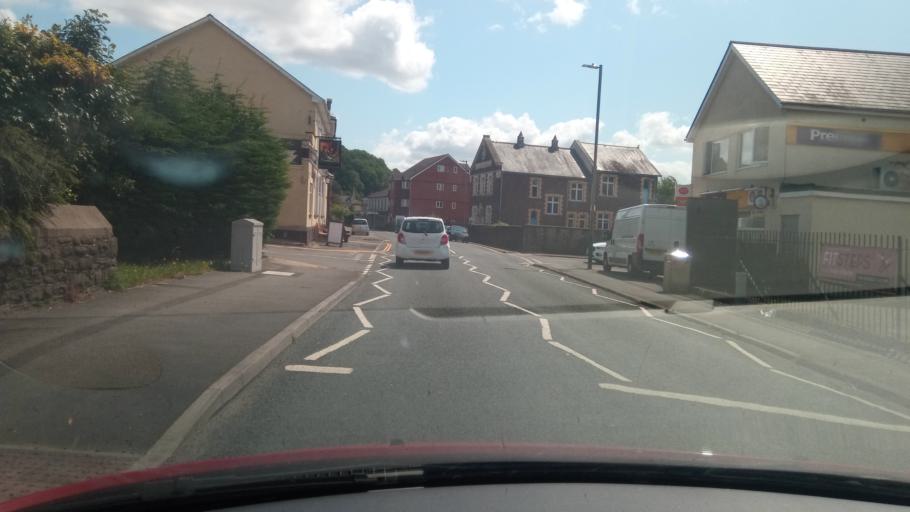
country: GB
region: Wales
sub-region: Caerphilly County Borough
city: Risca
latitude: 51.6137
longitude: -3.1042
